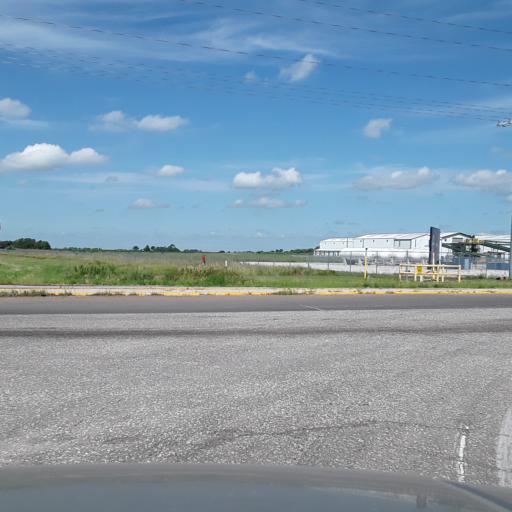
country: US
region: Nebraska
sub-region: York County
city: York
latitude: 40.9017
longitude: -97.4060
